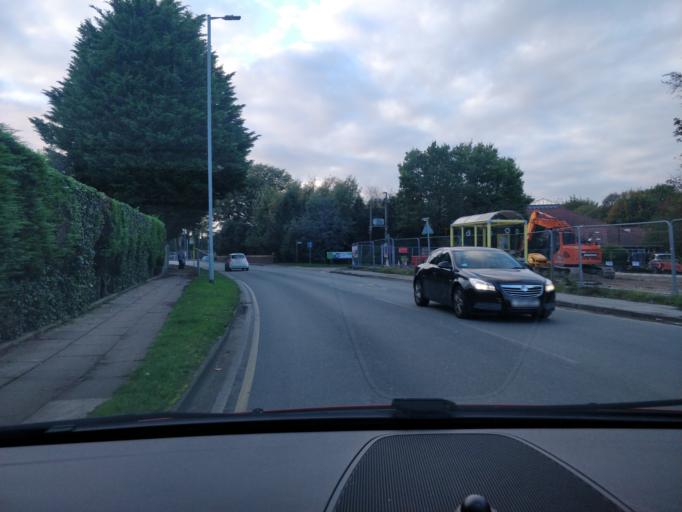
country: GB
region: England
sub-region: Sefton
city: Southport
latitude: 53.6331
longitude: -2.9735
